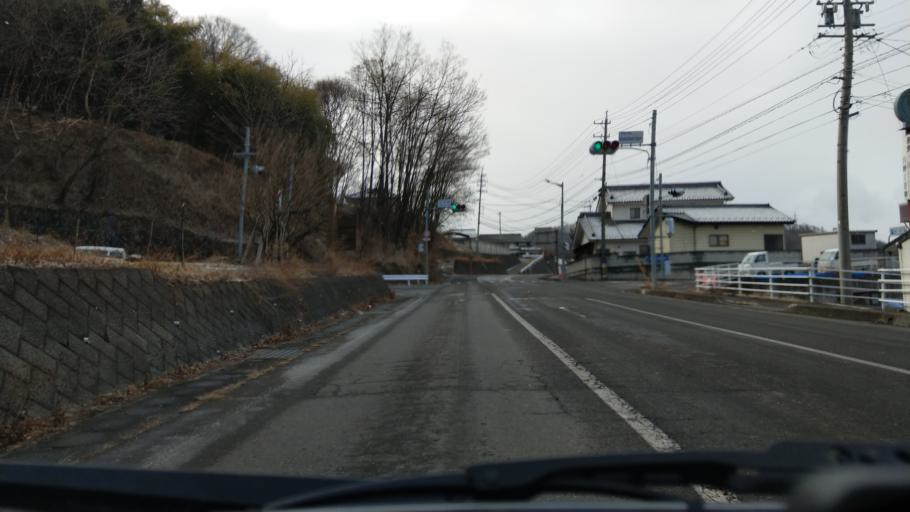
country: JP
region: Nagano
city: Kamimaruko
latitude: 36.3264
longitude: 138.3458
